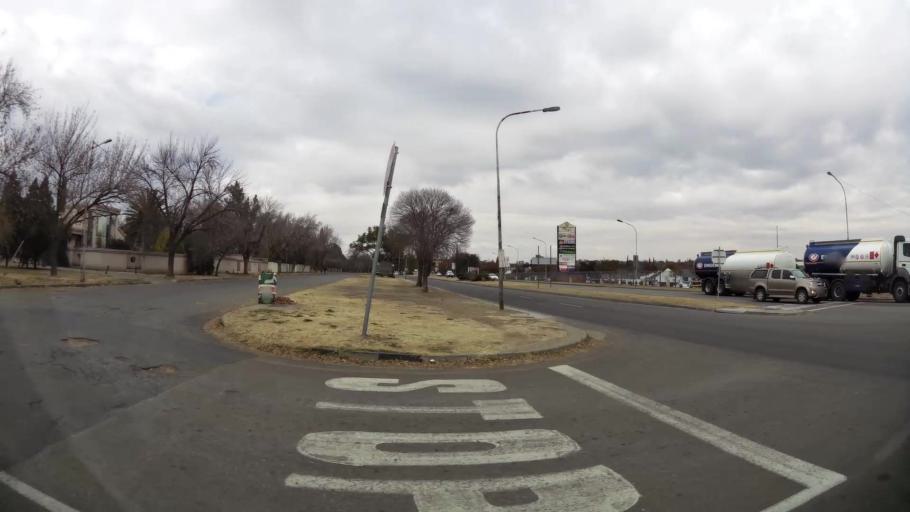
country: ZA
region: Orange Free State
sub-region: Fezile Dabi District Municipality
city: Kroonstad
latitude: -27.6763
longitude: 27.2399
